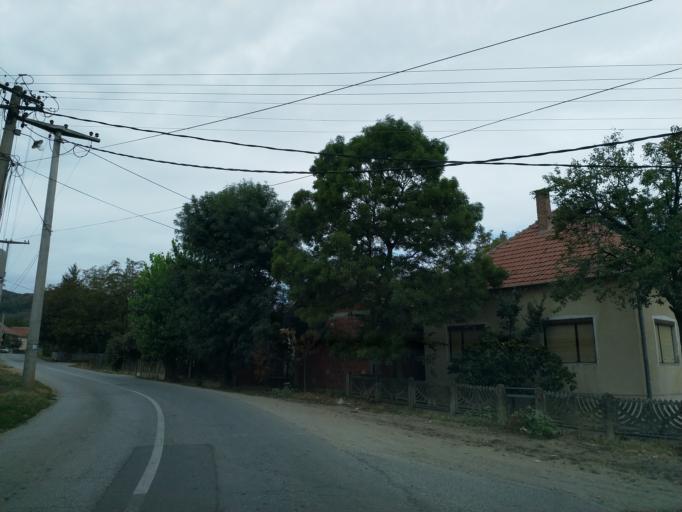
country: RS
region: Central Serbia
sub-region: Pomoravski Okrug
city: Paracin
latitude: 43.8373
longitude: 21.3218
